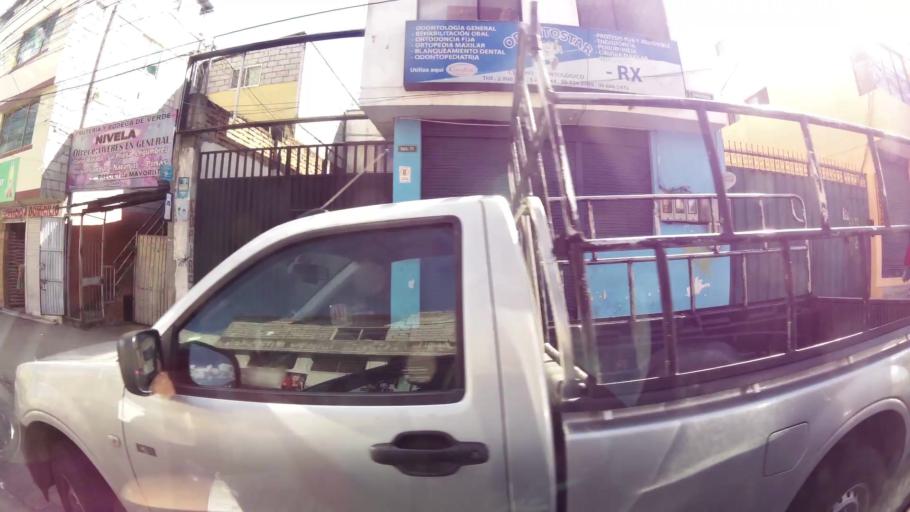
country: EC
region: Pichincha
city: Quito
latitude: -0.1271
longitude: -78.4697
